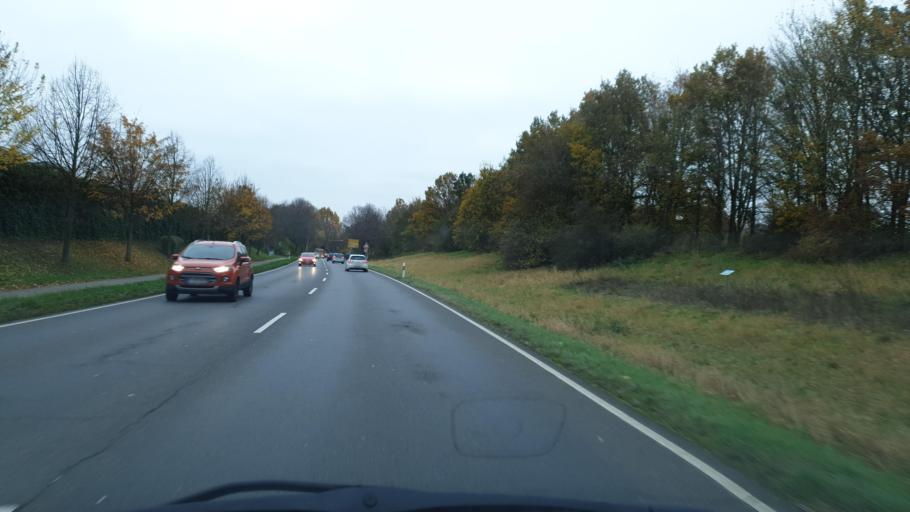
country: DE
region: North Rhine-Westphalia
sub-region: Regierungsbezirk Koln
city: Hurth
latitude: 50.8849
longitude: 6.8635
